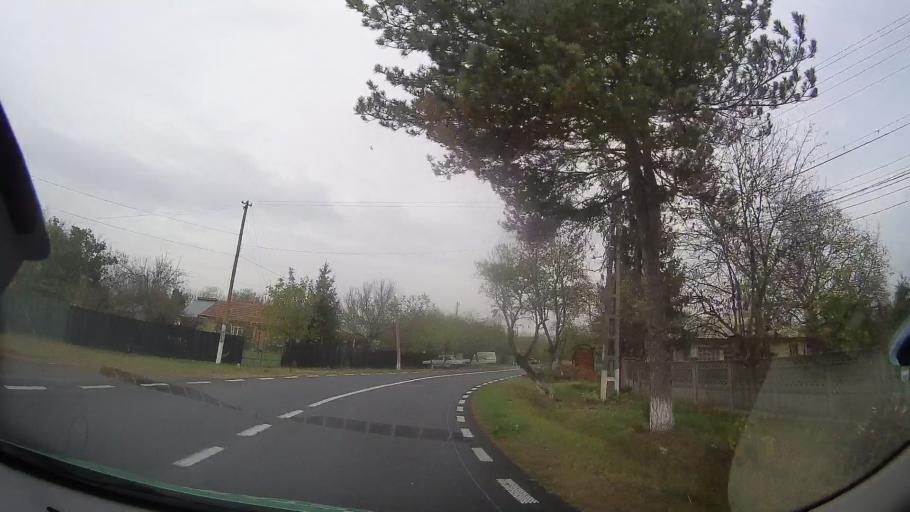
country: RO
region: Ilfov
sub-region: Comuna Nuci
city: Nuci
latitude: 44.7206
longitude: 26.2957
